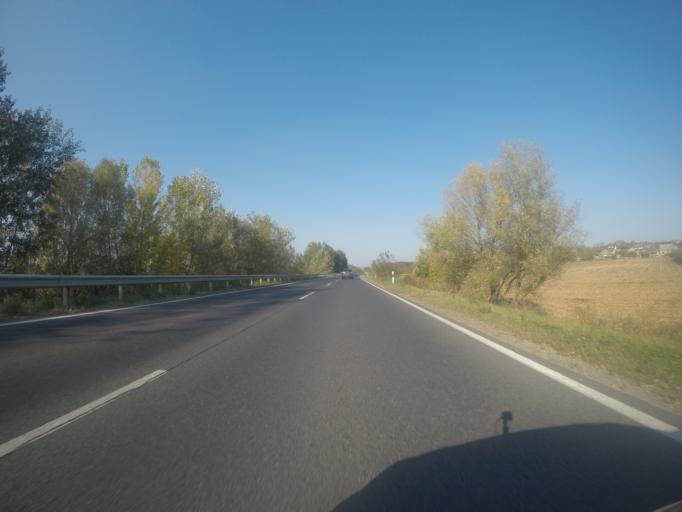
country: HU
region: Tolna
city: Dunafoldvar
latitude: 46.8219
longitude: 18.9062
